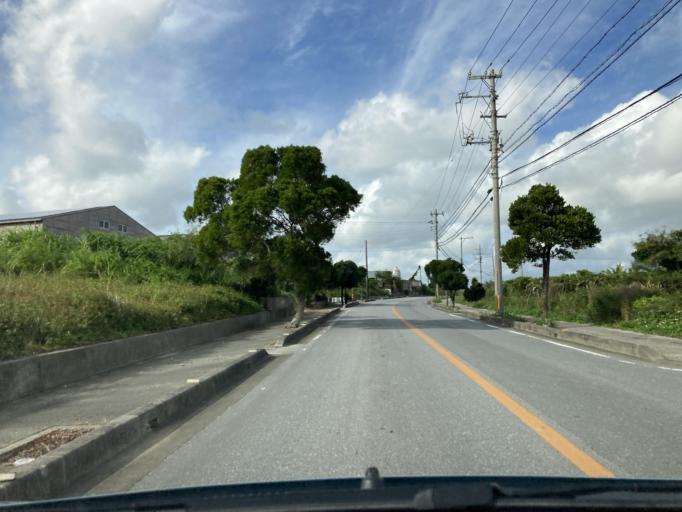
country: JP
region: Okinawa
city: Itoman
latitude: 26.1105
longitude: 127.7191
